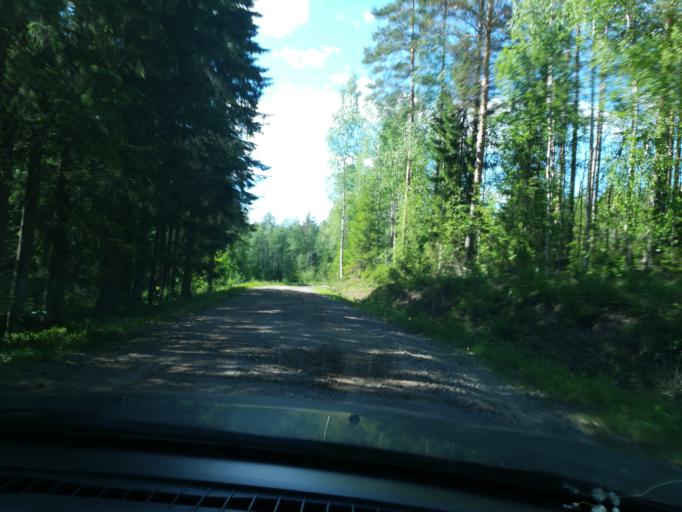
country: FI
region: Southern Savonia
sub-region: Mikkeli
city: Puumala
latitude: 61.6572
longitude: 28.1628
